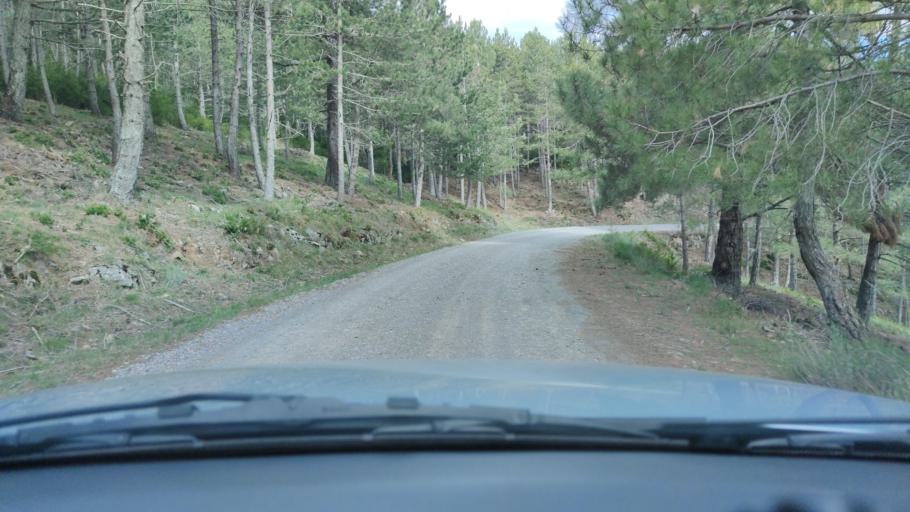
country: ES
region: Catalonia
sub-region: Provincia de Lleida
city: Coll de Nargo
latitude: 42.2479
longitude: 1.4065
